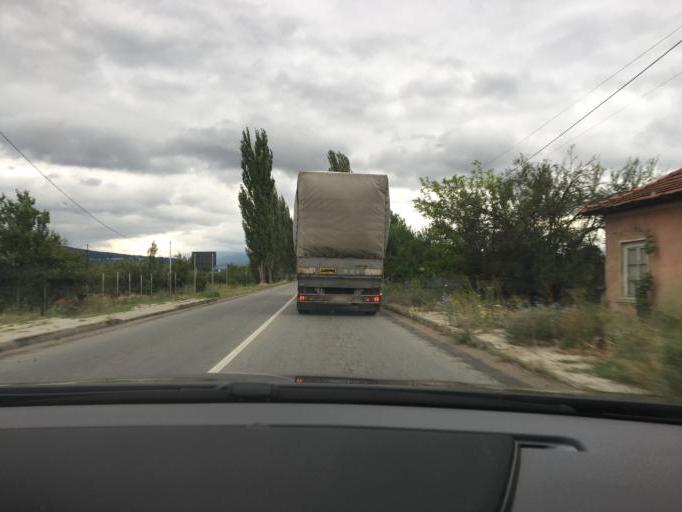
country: BG
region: Kyustendil
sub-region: Obshtina Kyustendil
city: Kyustendil
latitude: 42.2752
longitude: 22.7551
